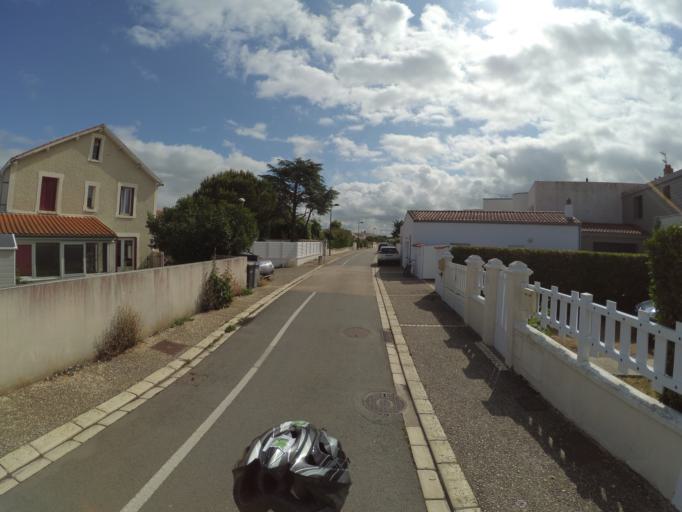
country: FR
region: Poitou-Charentes
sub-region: Departement de la Charente-Maritime
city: Angoulins
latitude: 46.1035
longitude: -1.1166
